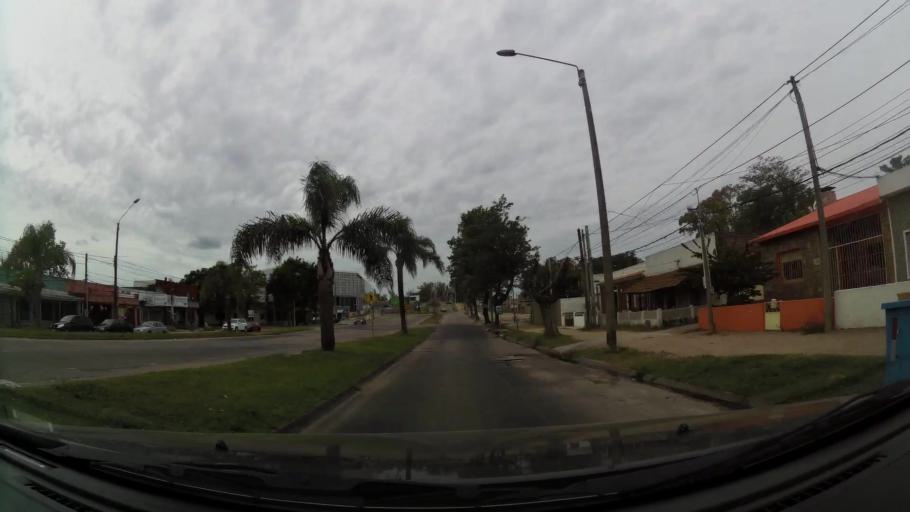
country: UY
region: Canelones
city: Las Piedras
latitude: -34.7263
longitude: -56.2057
